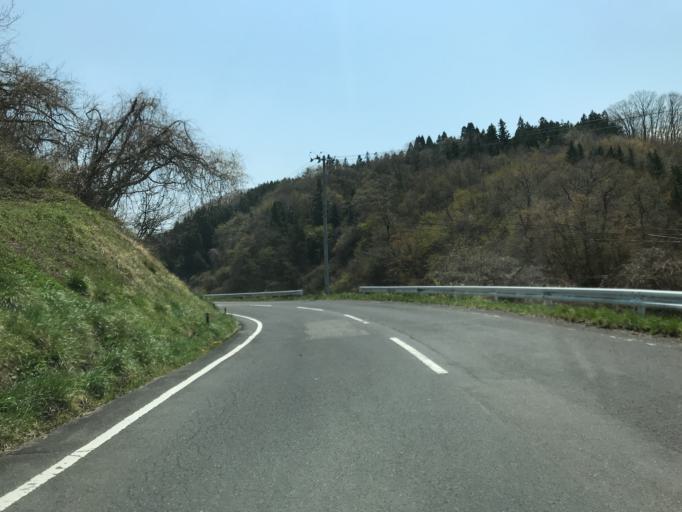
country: JP
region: Fukushima
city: Ishikawa
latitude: 37.0574
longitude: 140.4601
